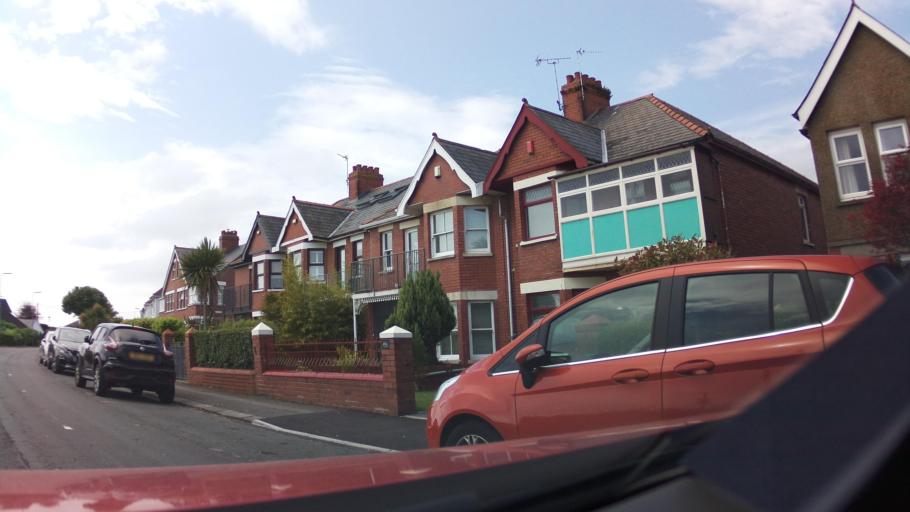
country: GB
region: Wales
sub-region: Vale of Glamorgan
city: Barry
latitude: 51.3920
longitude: -3.2887
